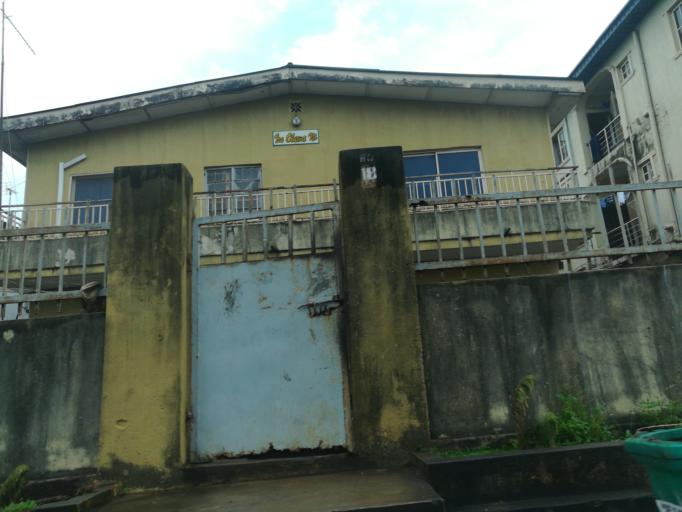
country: NG
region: Lagos
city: Oshodi
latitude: 6.5768
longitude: 3.3404
